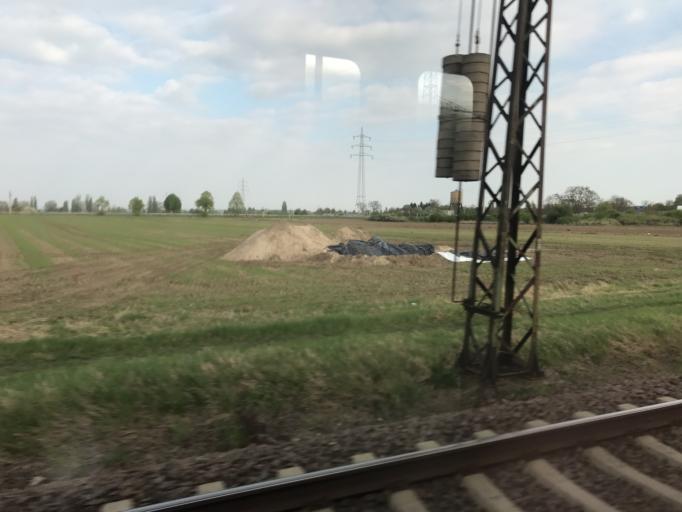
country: DE
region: Rheinland-Pfalz
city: Frankenthal
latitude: 49.5573
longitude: 8.3500
